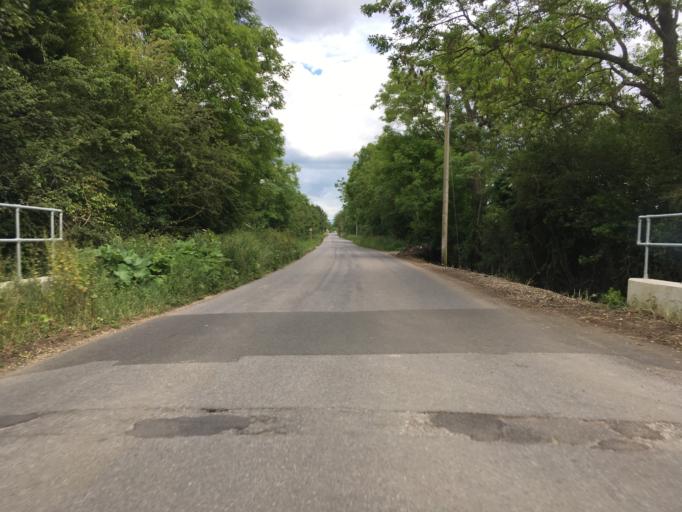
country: GB
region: England
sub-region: Wiltshire
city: Leigh
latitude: 51.6355
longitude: -1.8936
